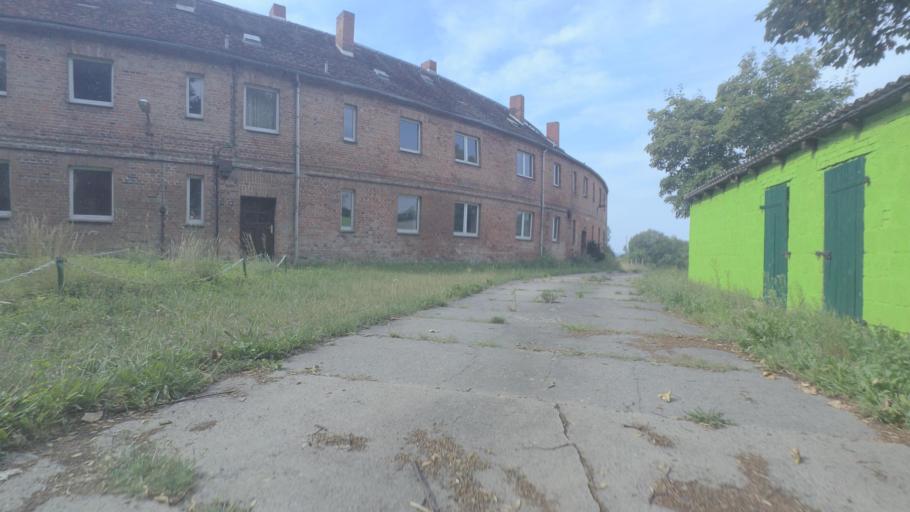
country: DE
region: Mecklenburg-Vorpommern
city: Gielow
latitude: 53.6484
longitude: 12.8313
